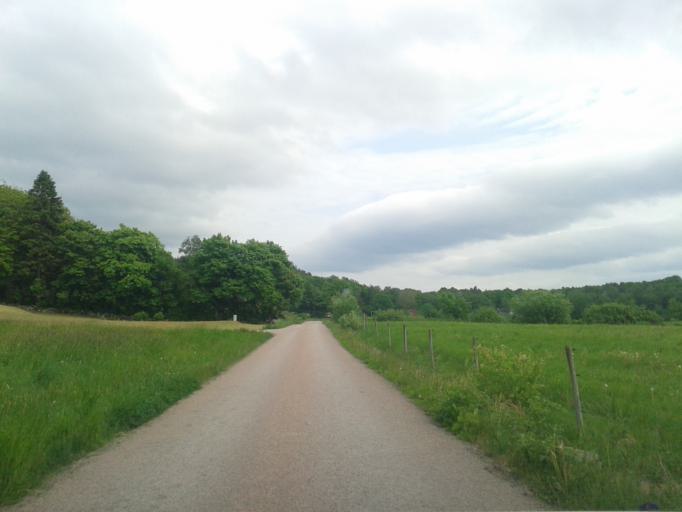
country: SE
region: Vaestra Goetaland
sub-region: Kungalvs Kommun
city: Kungalv
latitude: 57.9023
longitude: 11.9576
